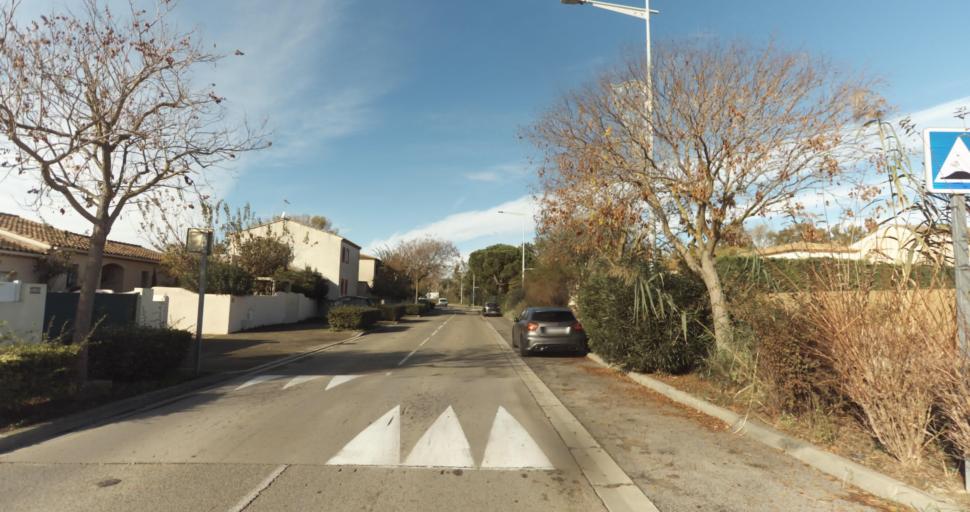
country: FR
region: Languedoc-Roussillon
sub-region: Departement du Gard
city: Aigues-Mortes
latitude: 43.5740
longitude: 4.1796
